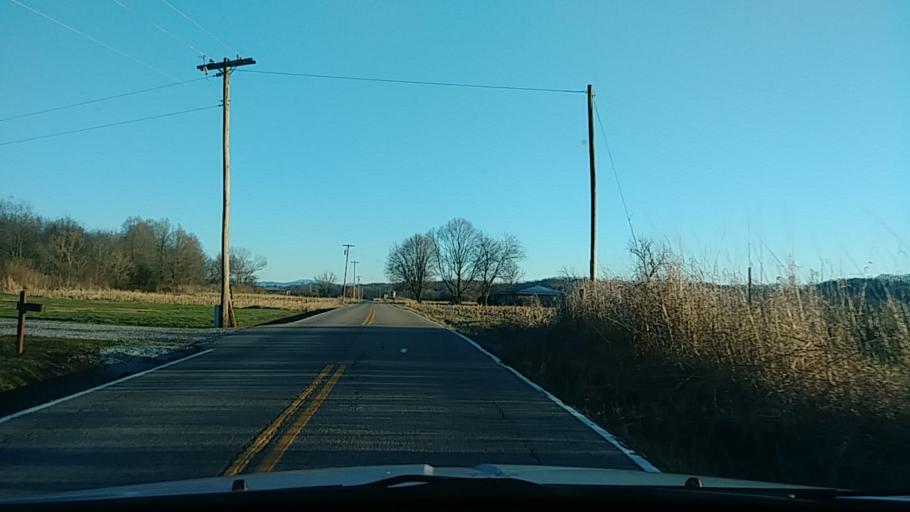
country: US
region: Tennessee
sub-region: Jefferson County
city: White Pine
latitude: 36.1577
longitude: -83.1618
